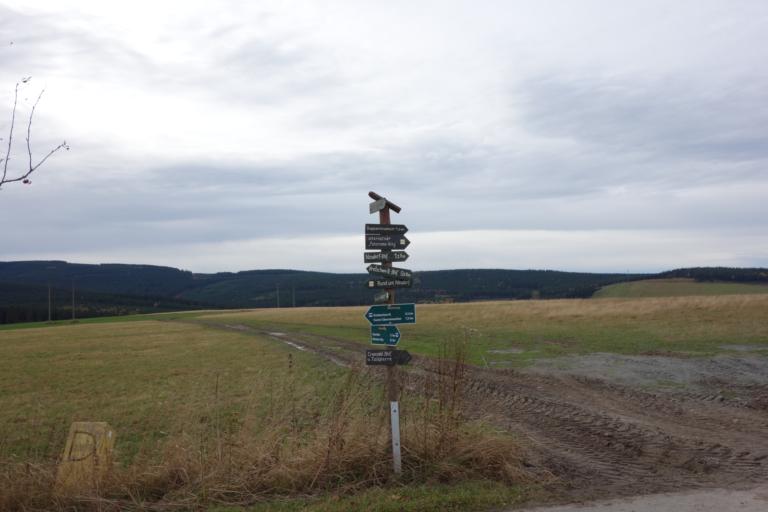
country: CZ
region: Ustecky
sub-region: Okres Chomutov
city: Vejprty
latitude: 50.4705
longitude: 12.9848
